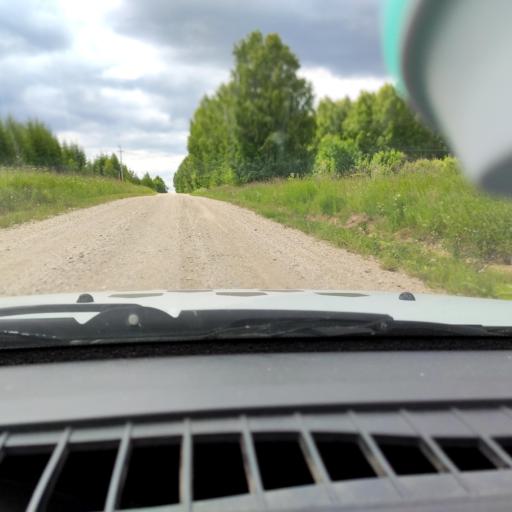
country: RU
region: Perm
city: Suksun
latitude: 57.2135
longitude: 57.6810
